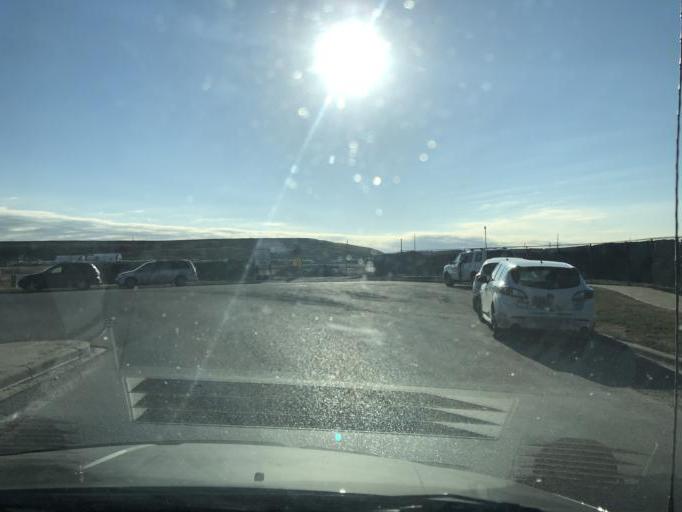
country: CA
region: Alberta
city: Calgary
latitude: 50.9594
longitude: -114.0078
